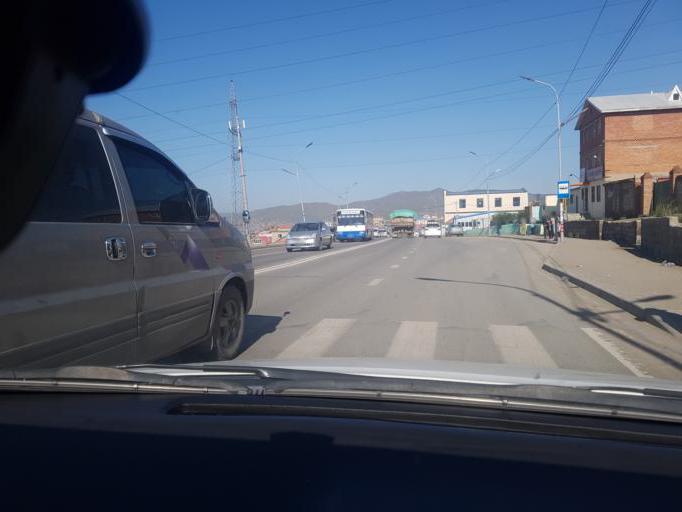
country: MN
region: Ulaanbaatar
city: Ulaanbaatar
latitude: 47.9510
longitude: 106.8595
